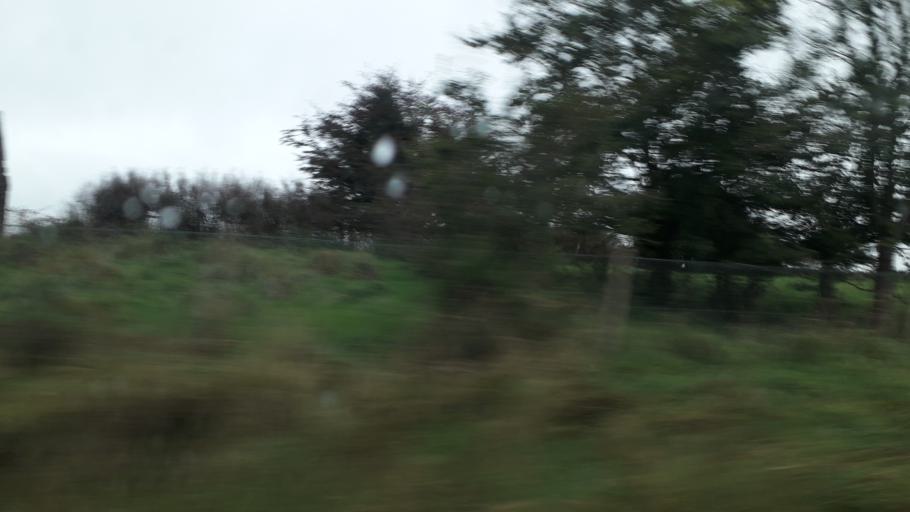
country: IE
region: Connaught
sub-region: Roscommon
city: Roscommon
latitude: 53.7670
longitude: -8.2048
